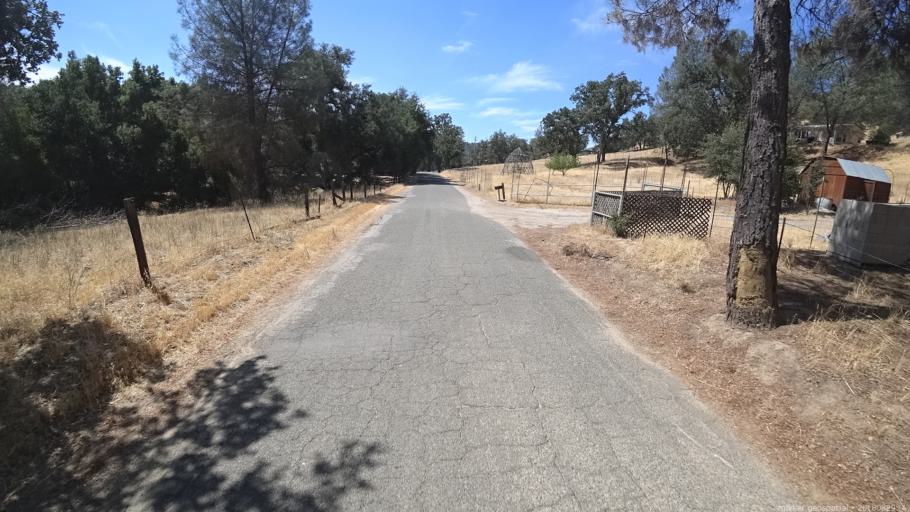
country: US
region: California
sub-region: San Luis Obispo County
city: Lake Nacimiento
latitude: 35.8187
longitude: -121.0756
